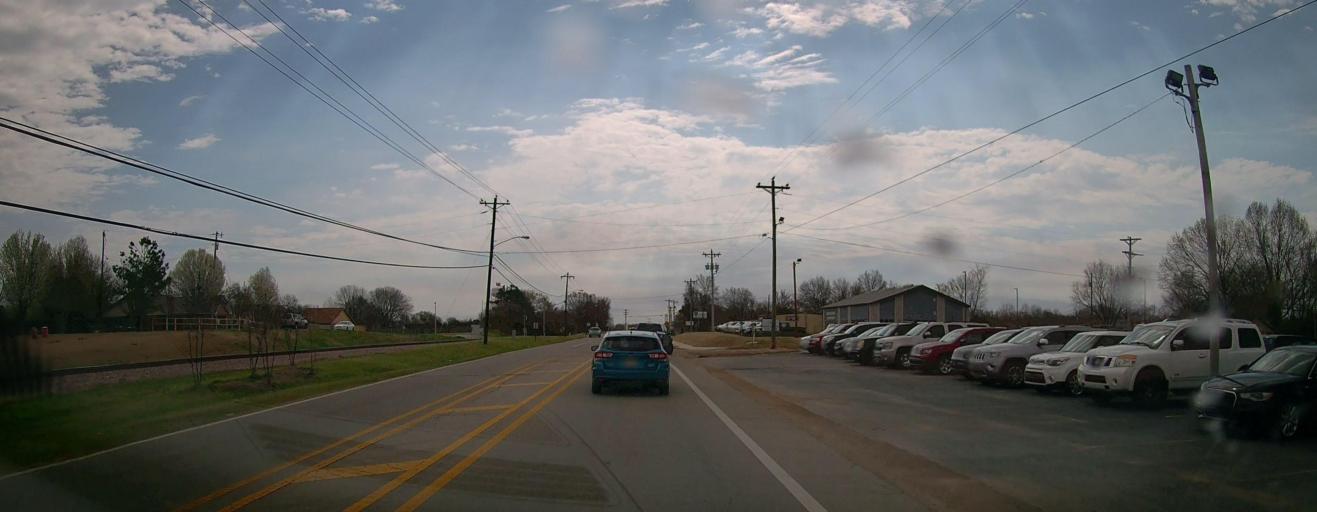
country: US
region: Mississippi
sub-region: De Soto County
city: Olive Branch
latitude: 34.9572
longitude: -89.8187
